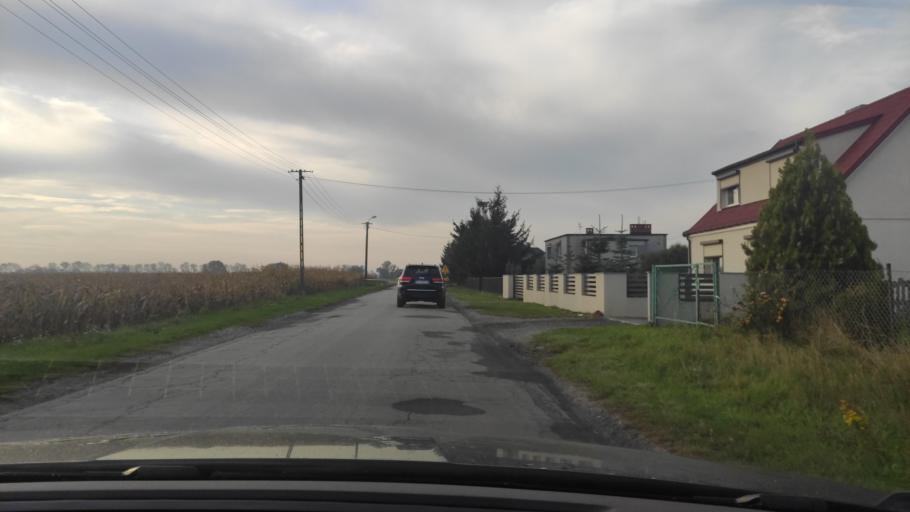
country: PL
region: Greater Poland Voivodeship
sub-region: Powiat poznanski
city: Kleszczewo
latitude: 52.3755
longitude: 17.1665
